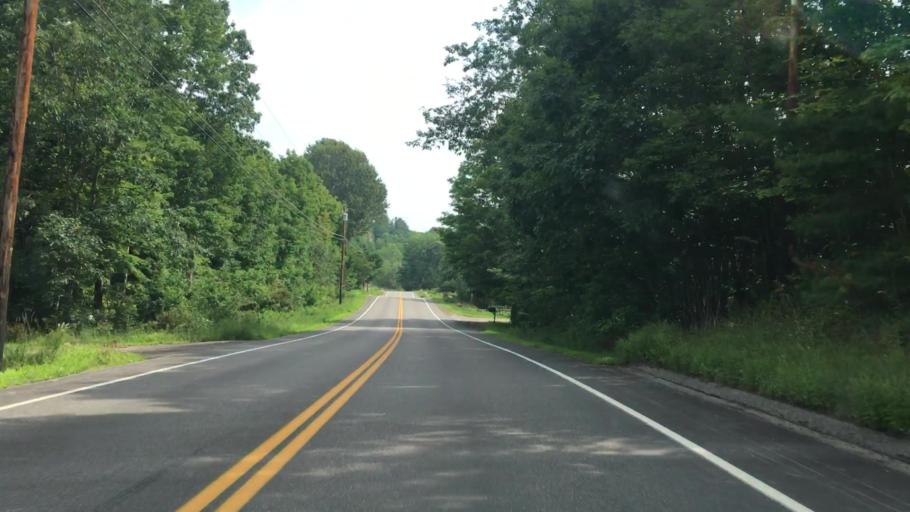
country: US
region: Maine
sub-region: Kennebec County
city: Windsor
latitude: 44.3355
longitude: -69.5821
